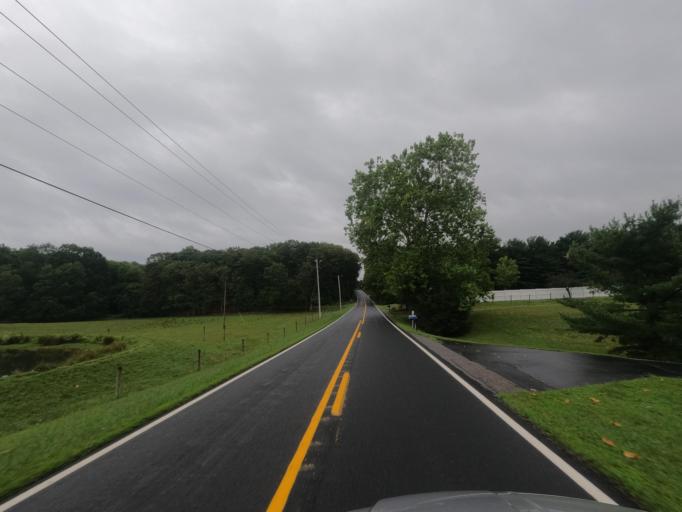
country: US
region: Maryland
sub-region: Washington County
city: Wilson-Conococheague
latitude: 39.6220
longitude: -77.9844
